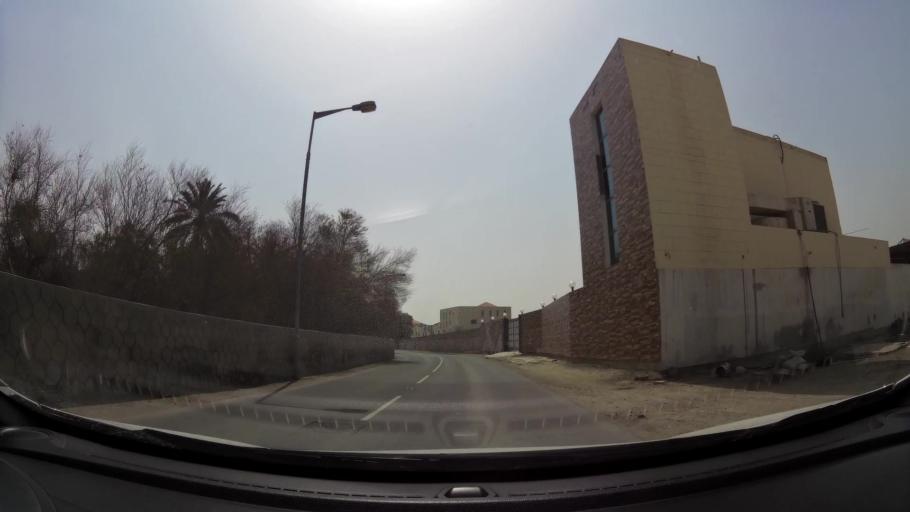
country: BH
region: Manama
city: Jidd Hafs
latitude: 26.2226
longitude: 50.5045
